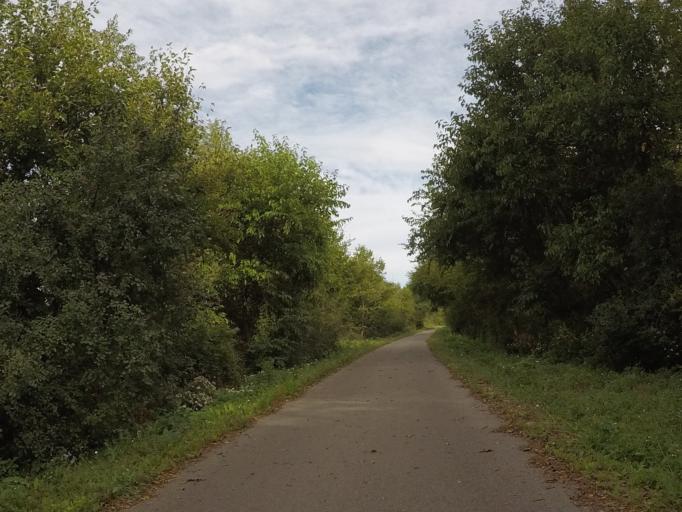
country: US
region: Wisconsin
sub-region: Sauk County
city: Prairie du Sac
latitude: 43.3285
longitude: -89.7490
